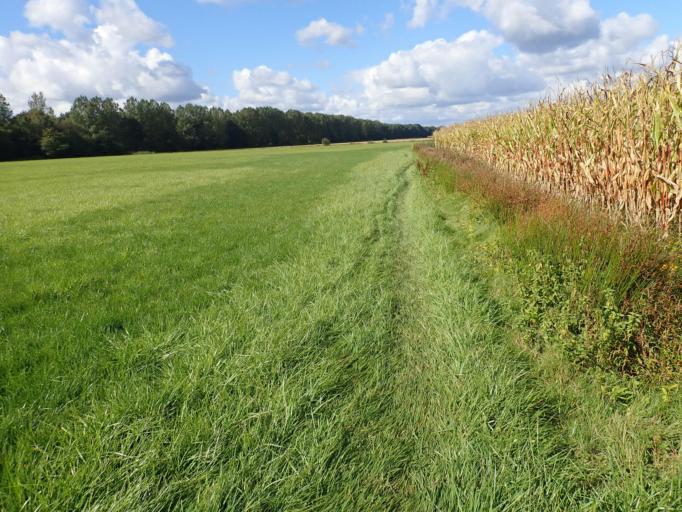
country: BE
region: Flanders
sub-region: Provincie Antwerpen
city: Hulshout
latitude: 51.0879
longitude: 4.8079
